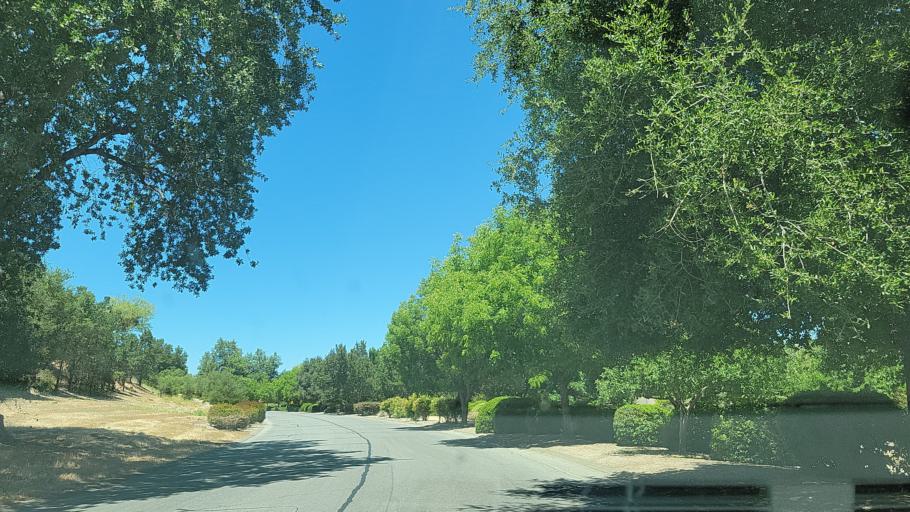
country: US
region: California
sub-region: San Luis Obispo County
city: Atascadero
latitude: 35.5133
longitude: -120.6737
